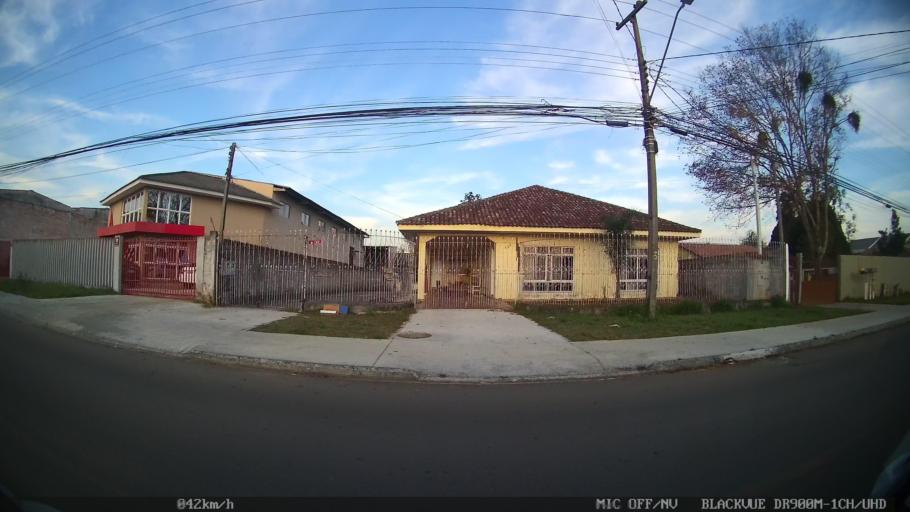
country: BR
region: Parana
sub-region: Pinhais
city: Pinhais
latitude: -25.4520
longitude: -49.1811
